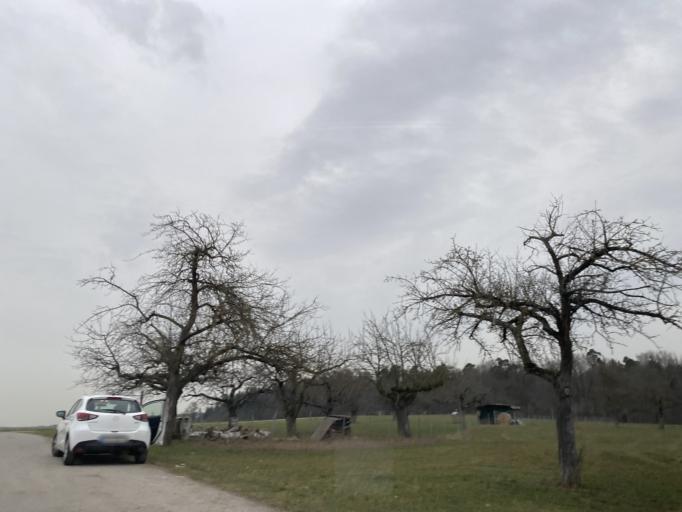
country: DE
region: Baden-Wuerttemberg
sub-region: Regierungsbezirk Stuttgart
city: Eberdingen
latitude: 48.8854
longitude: 8.9314
